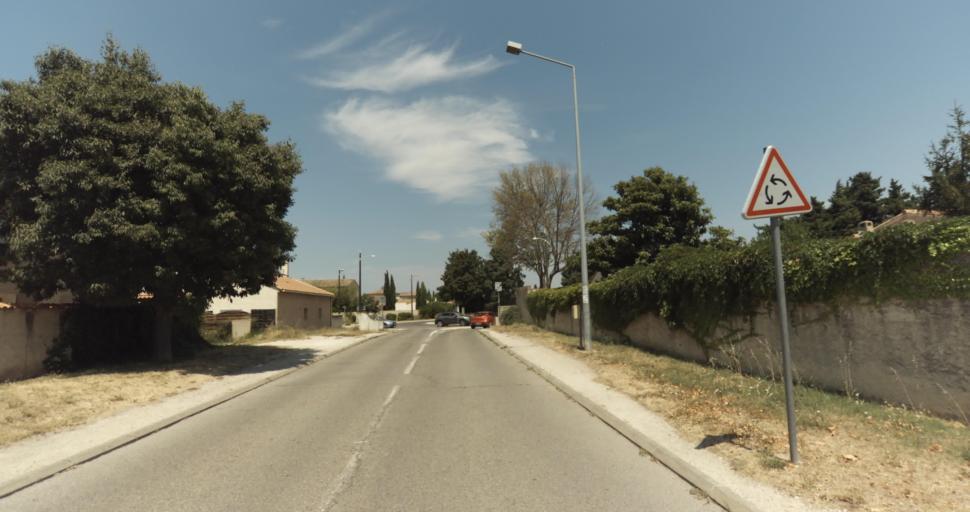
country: FR
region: Provence-Alpes-Cote d'Azur
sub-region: Departement du Vaucluse
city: Monteux
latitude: 44.0309
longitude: 4.9841
